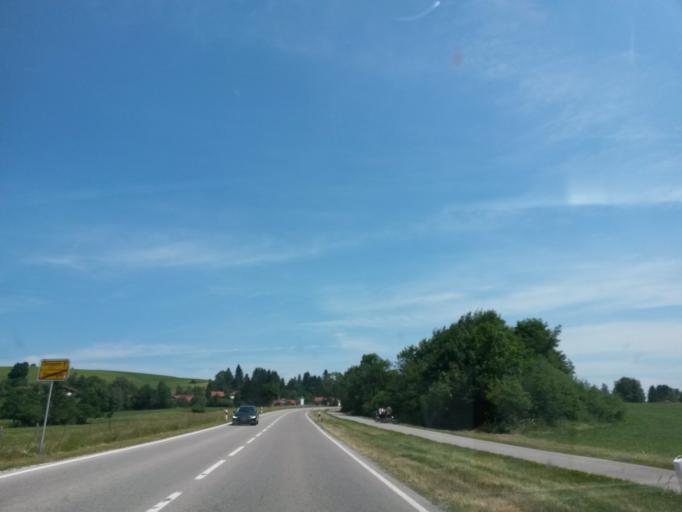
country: DE
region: Bavaria
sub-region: Swabia
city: Halblech
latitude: 47.6463
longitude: 10.8291
